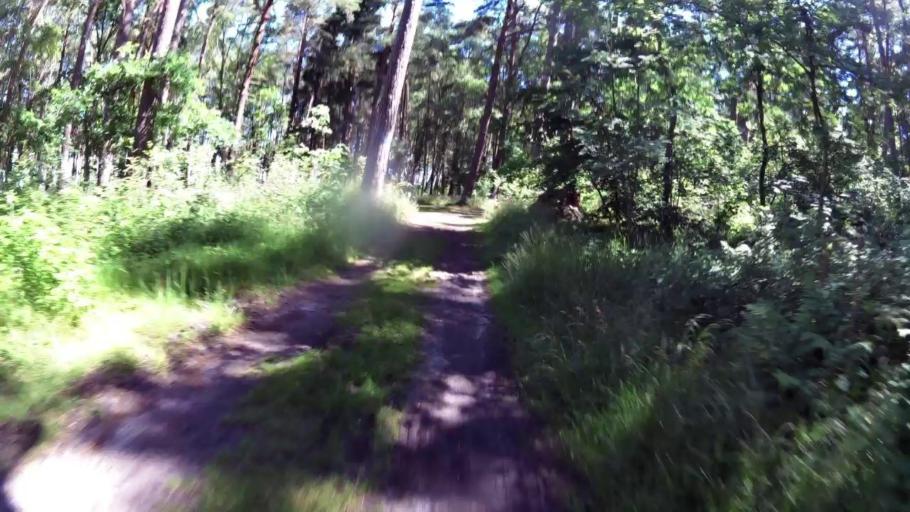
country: PL
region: West Pomeranian Voivodeship
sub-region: Powiat gryficki
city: Pobierowo
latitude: 54.0452
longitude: 14.8498
